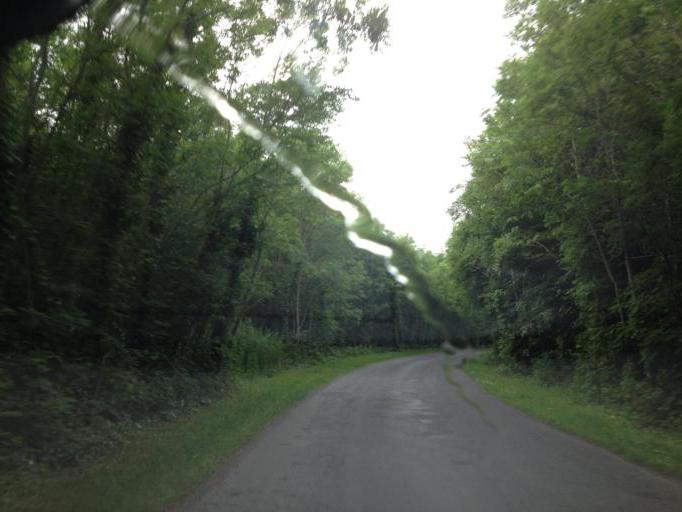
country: IE
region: Connaught
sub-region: Sligo
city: Sligo
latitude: 54.2620
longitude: -8.4313
